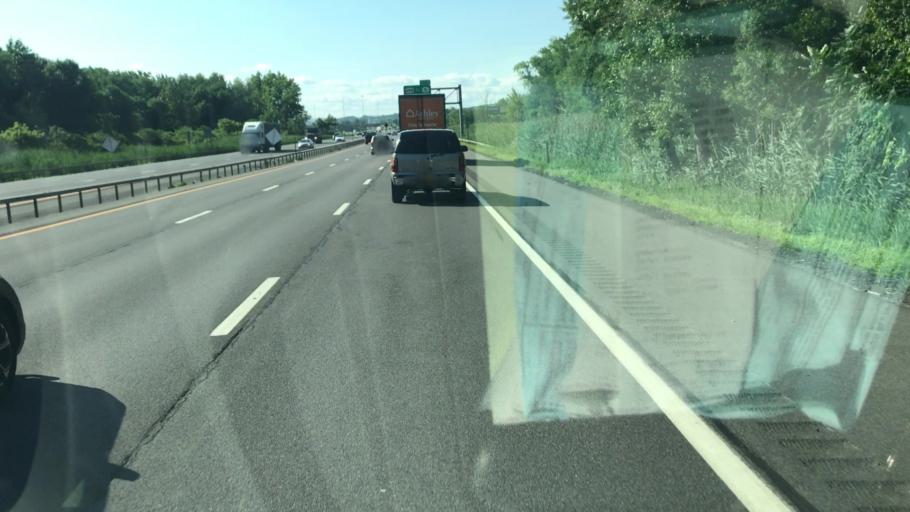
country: US
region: New York
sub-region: Onondaga County
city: Lakeland
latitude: 43.0919
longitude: -76.2342
